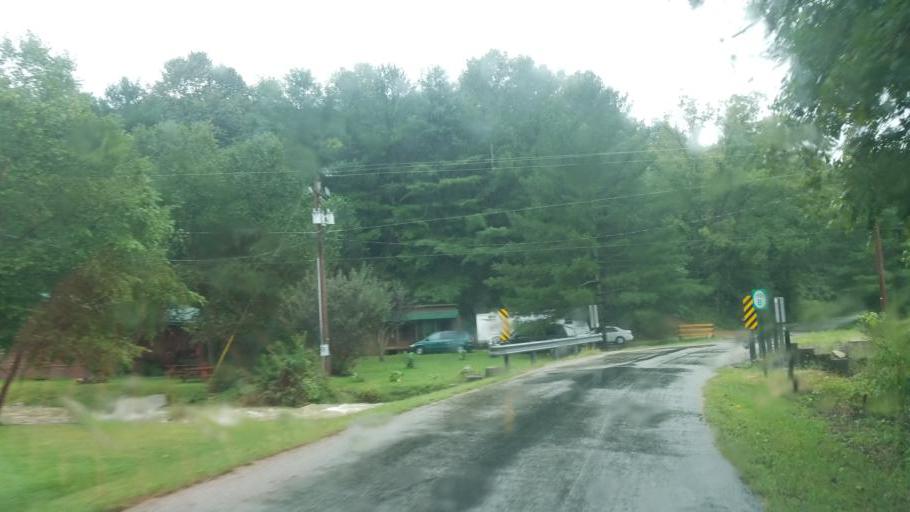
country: US
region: Kentucky
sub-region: Lewis County
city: Vanceburg
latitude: 38.7763
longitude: -83.2564
